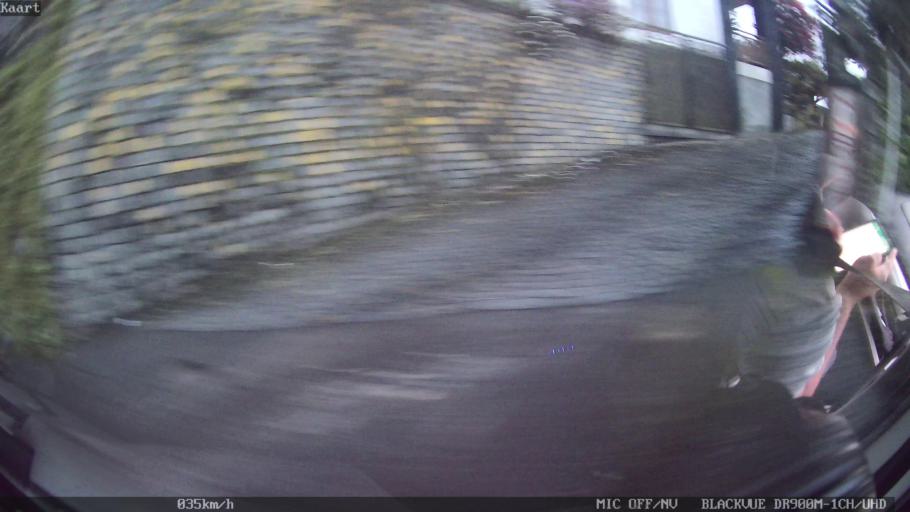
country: ID
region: Bali
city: Banjar Badung Tengah
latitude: -8.5116
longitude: 115.2009
